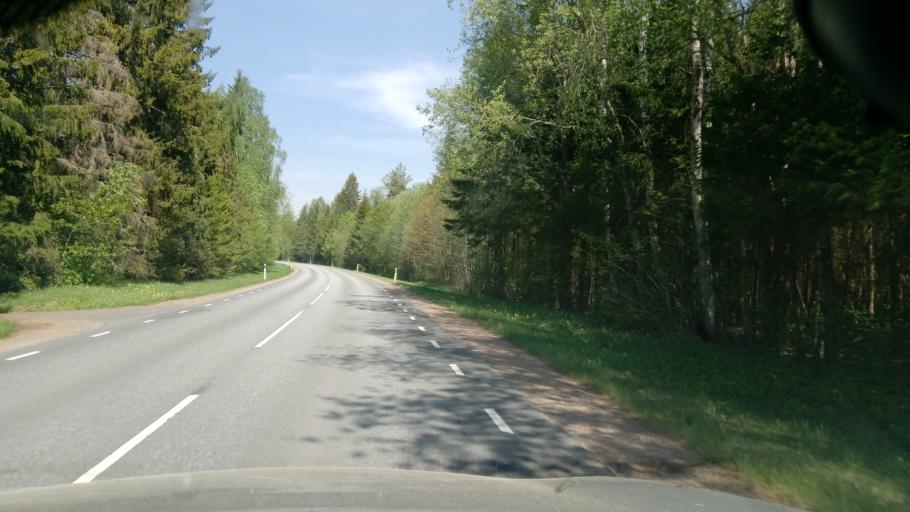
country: EE
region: Laeaene-Virumaa
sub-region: Kadrina vald
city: Kadrina
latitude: 59.3873
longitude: 26.0168
